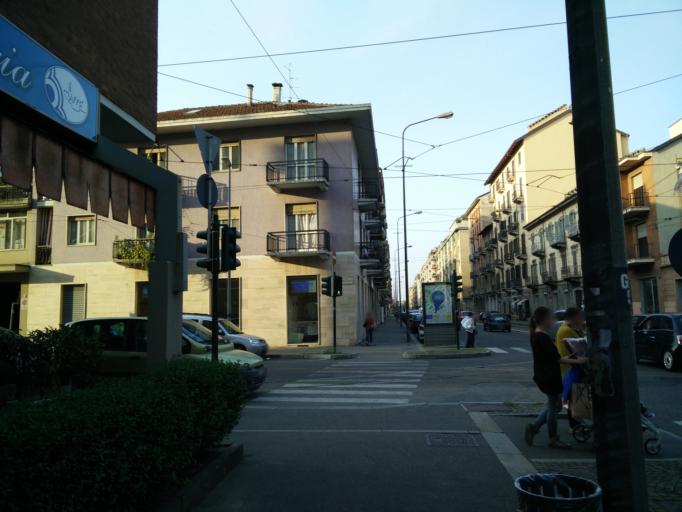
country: IT
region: Piedmont
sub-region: Provincia di Torino
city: Moncalieri
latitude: 45.0286
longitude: 7.6679
